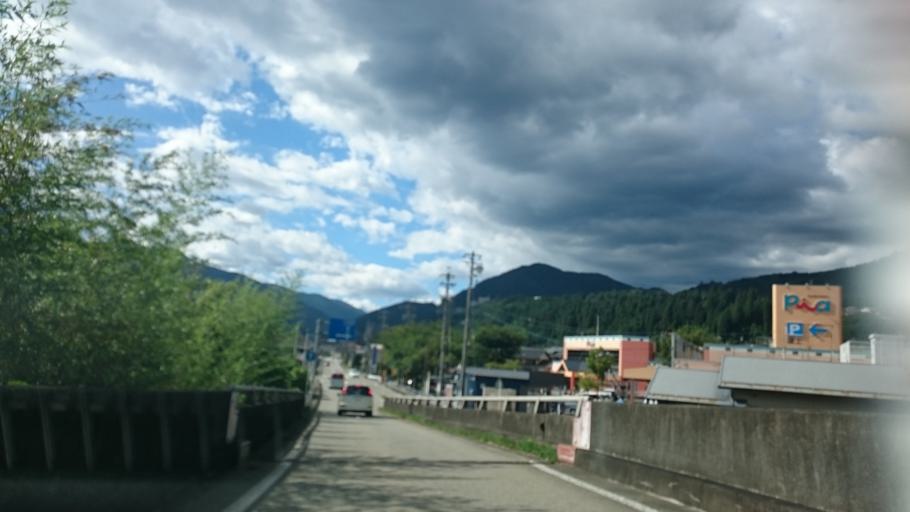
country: JP
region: Gifu
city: Gujo
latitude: 35.7941
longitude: 137.2575
